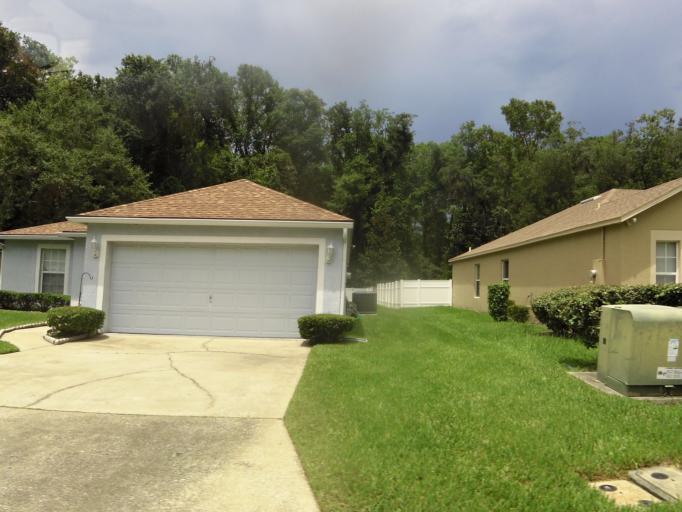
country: US
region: Florida
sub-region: Duval County
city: Jacksonville
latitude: 30.4264
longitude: -81.7262
